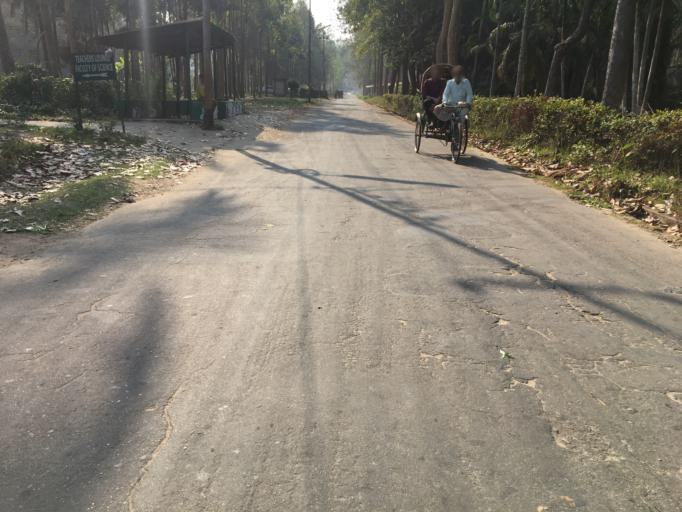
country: BD
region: Chittagong
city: Chittagong
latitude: 22.4712
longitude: 91.7871
